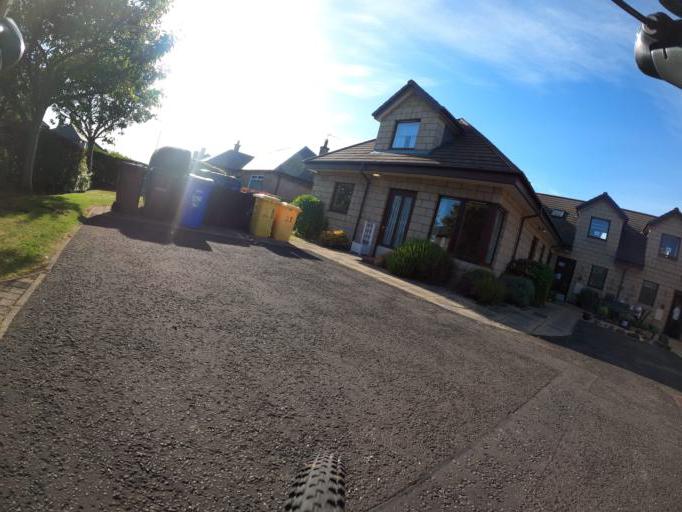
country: GB
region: Scotland
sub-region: Edinburgh
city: Edinburgh
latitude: 55.9757
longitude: -3.2283
